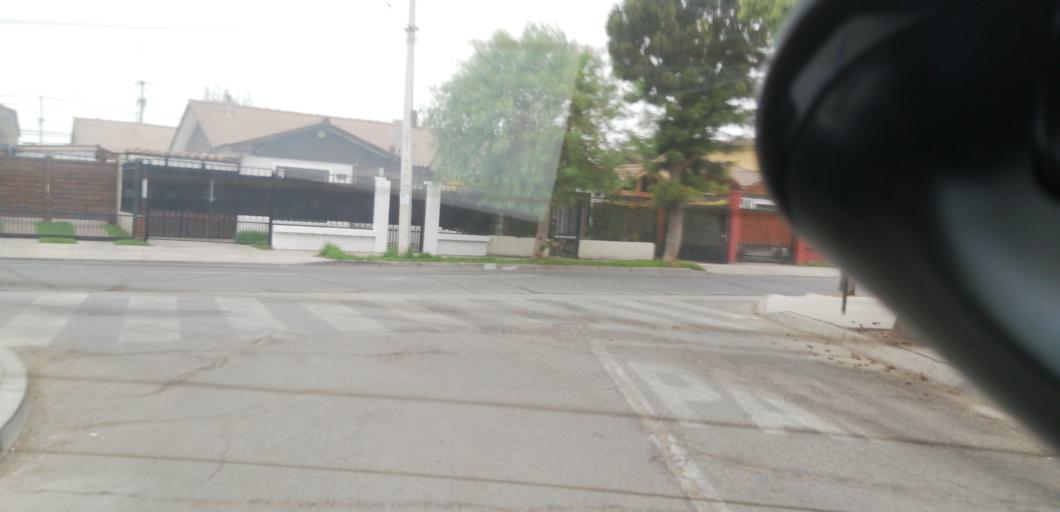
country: CL
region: Santiago Metropolitan
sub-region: Provincia de Santiago
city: Lo Prado
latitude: -33.4526
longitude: -70.7701
